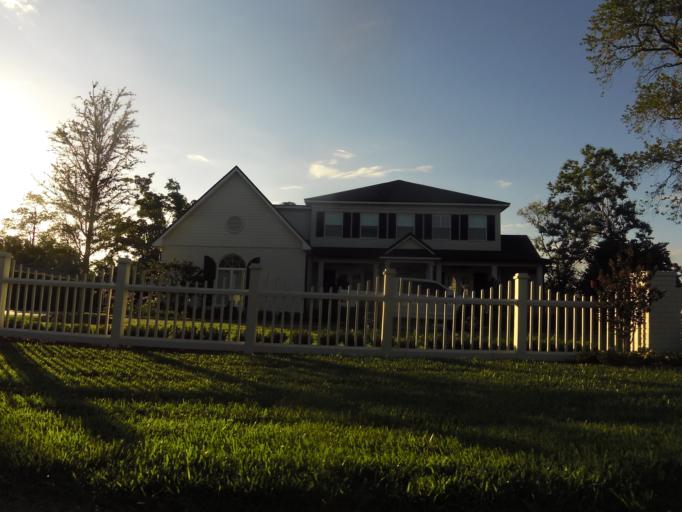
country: US
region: Florida
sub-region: Clay County
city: Orange Park
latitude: 30.2528
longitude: -81.6959
